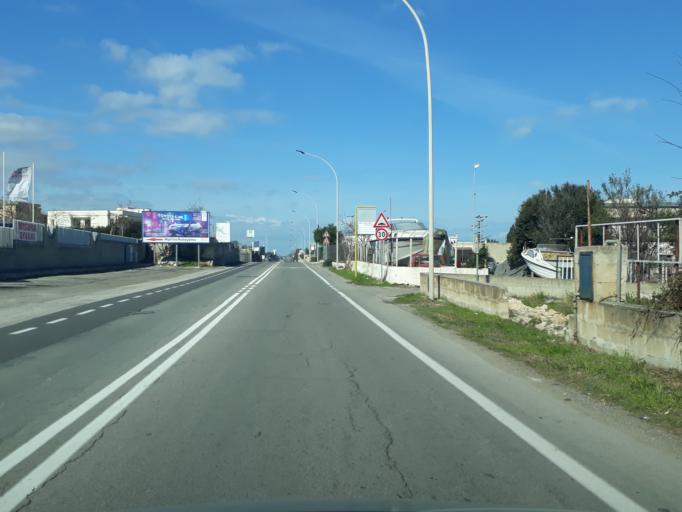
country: IT
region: Apulia
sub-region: Provincia di Bari
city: Monopoli
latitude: 40.9695
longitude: 17.2670
